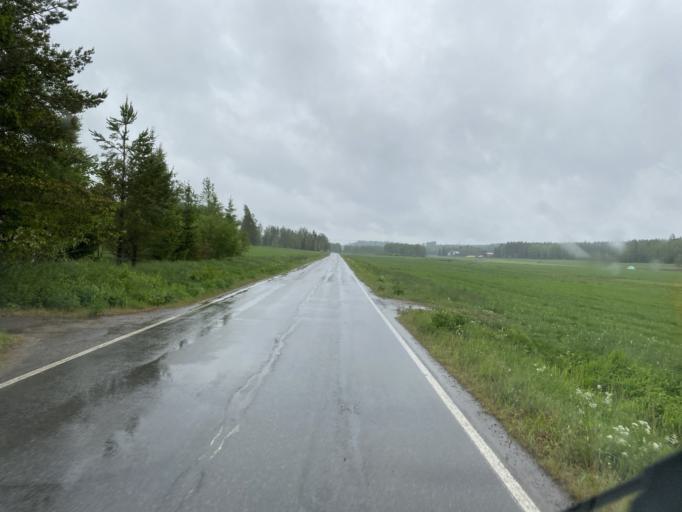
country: FI
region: Haeme
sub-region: Forssa
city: Humppila
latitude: 61.0437
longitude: 23.3880
